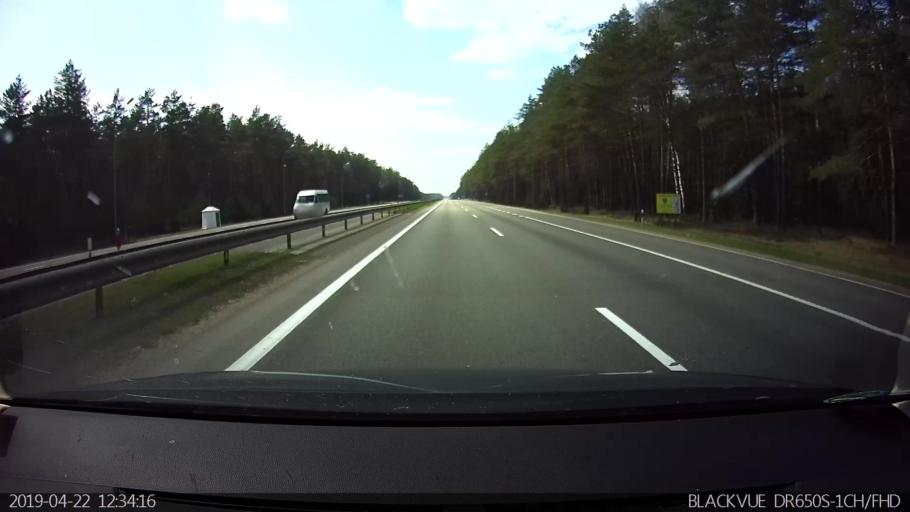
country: BY
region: Minsk
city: Enyerhyetykaw
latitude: 53.5453
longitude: 26.9313
